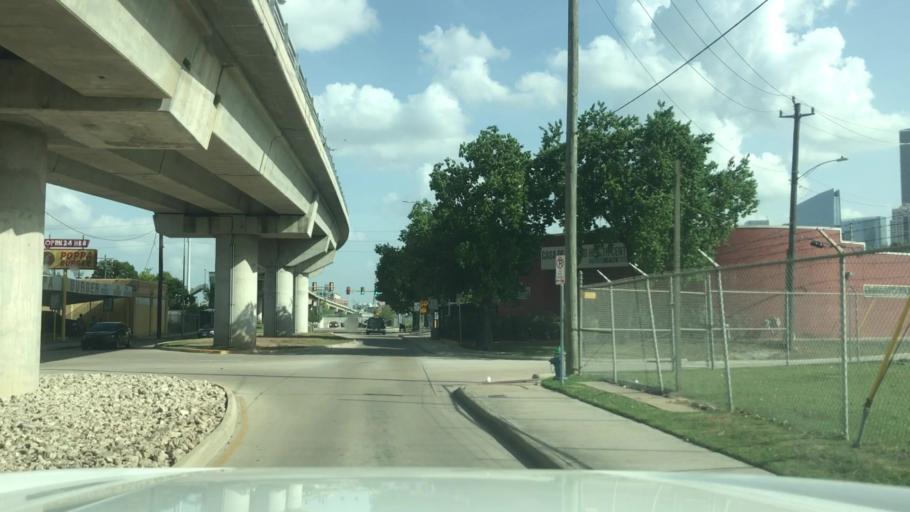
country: US
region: Texas
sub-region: Harris County
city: Houston
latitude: 29.7745
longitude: -95.3610
